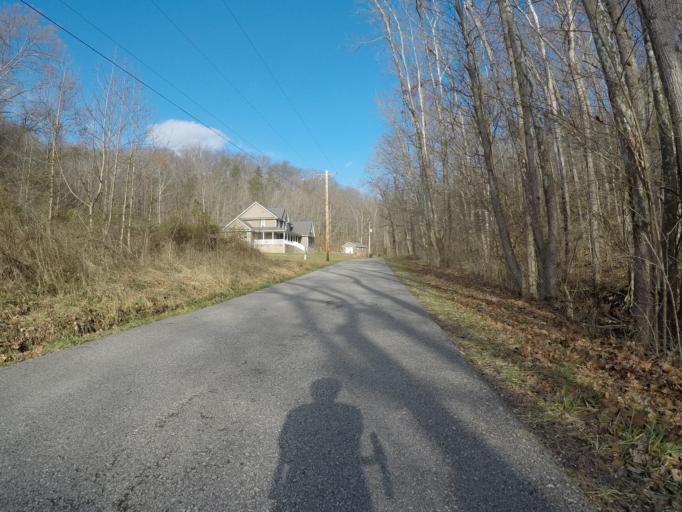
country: US
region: West Virginia
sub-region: Cabell County
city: Pea Ridge
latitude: 38.4254
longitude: -82.3408
